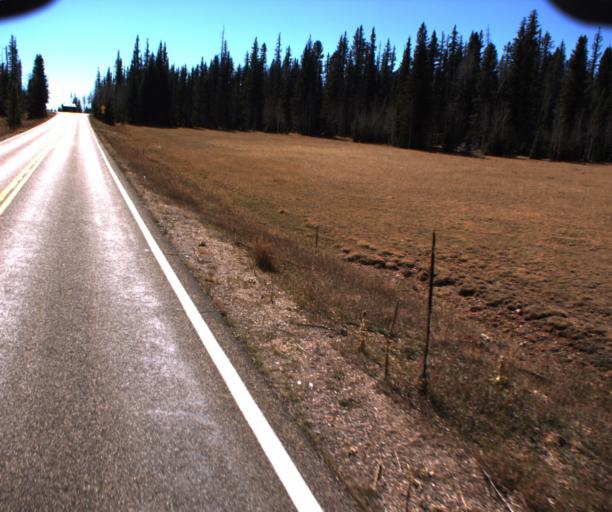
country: US
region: Arizona
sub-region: Coconino County
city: Grand Canyon
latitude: 36.3373
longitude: -112.1167
